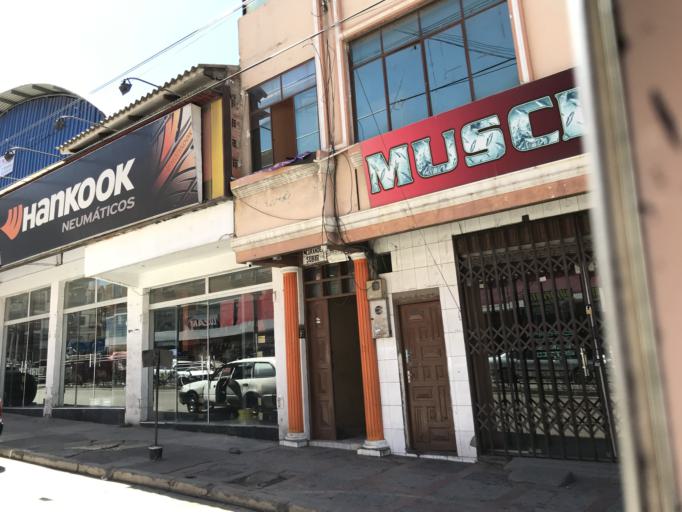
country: BO
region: Chuquisaca
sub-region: Provincia Oropeza
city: Huata
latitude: -19.0333
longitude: -65.2447
